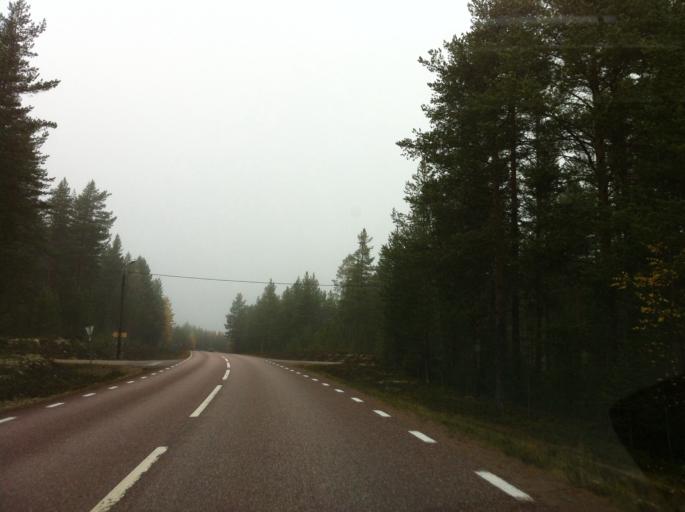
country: NO
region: Hedmark
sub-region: Trysil
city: Innbygda
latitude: 61.7452
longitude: 12.9733
